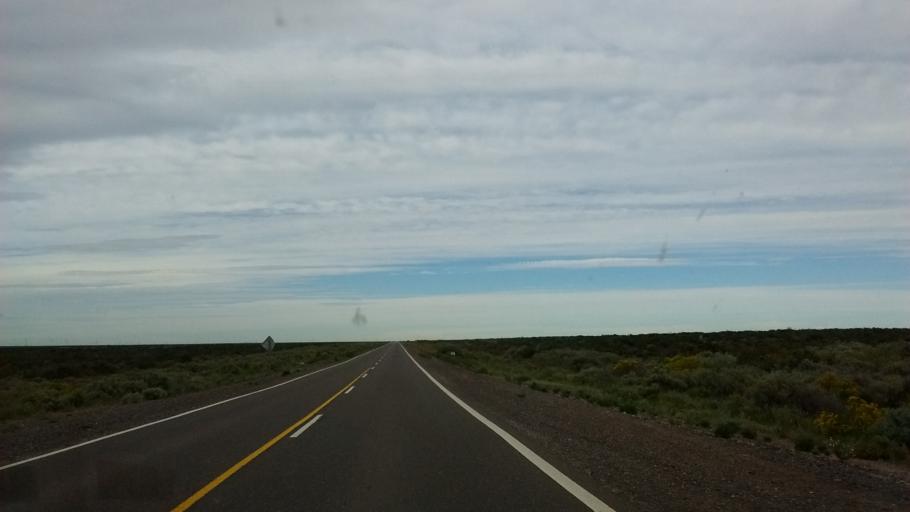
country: AR
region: Rio Negro
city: Contraalmirante Cordero
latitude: -38.4682
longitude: -68.0489
